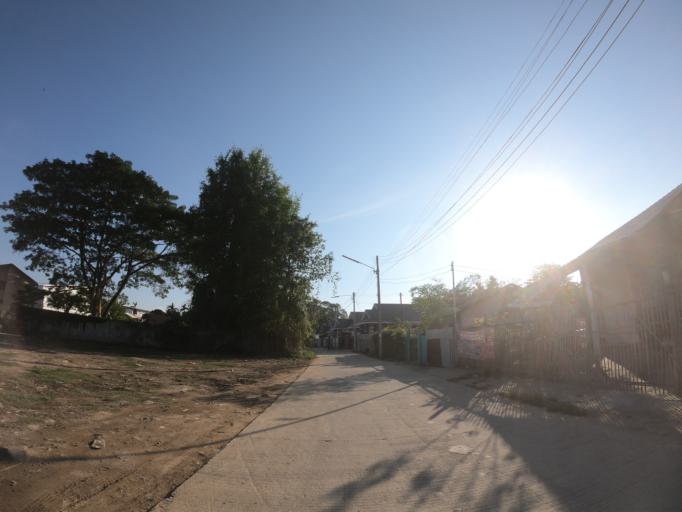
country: TH
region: Chiang Mai
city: Chiang Mai
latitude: 18.7414
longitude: 98.9803
